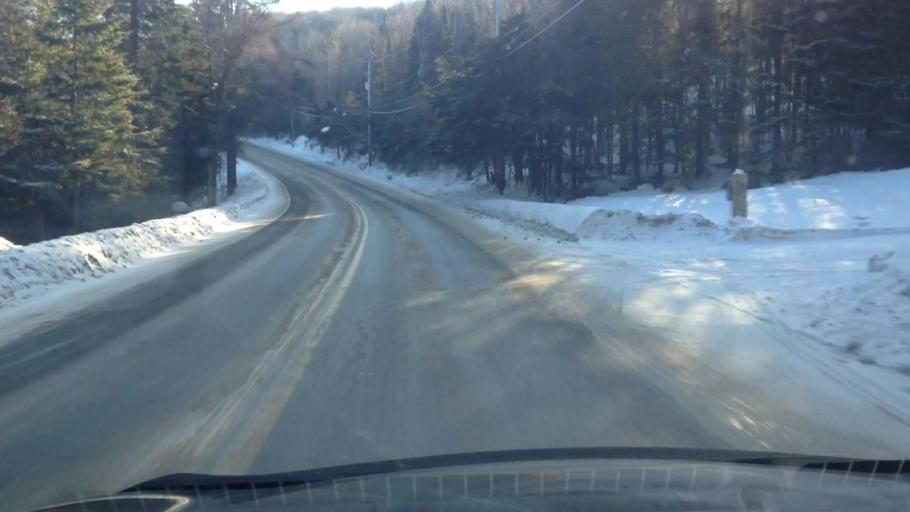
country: CA
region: Quebec
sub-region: Laurentides
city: Sainte-Agathe-des-Monts
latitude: 45.9163
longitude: -74.3728
